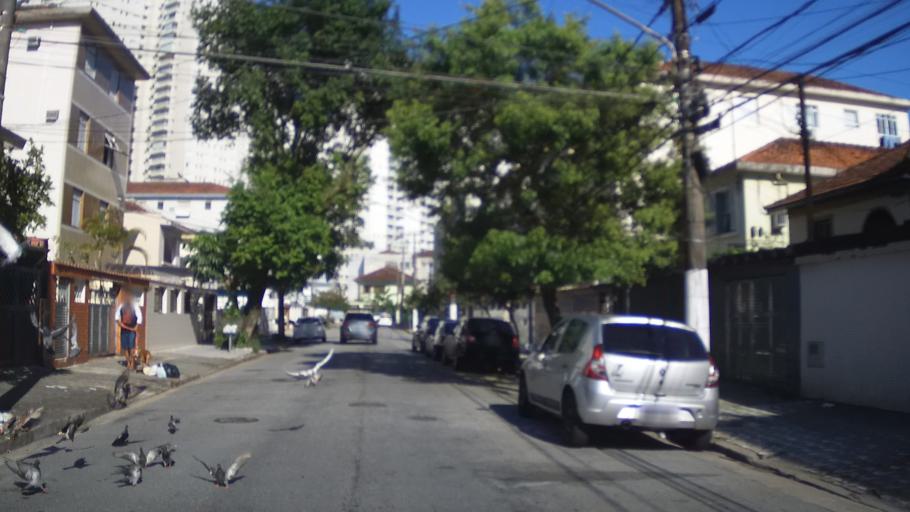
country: BR
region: Sao Paulo
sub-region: Santos
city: Santos
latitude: -23.9583
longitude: -46.3474
